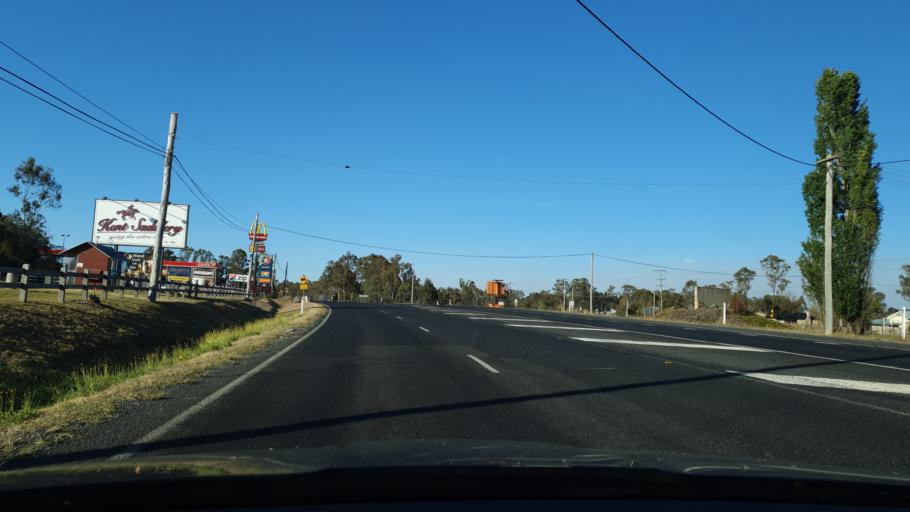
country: AU
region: Queensland
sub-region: Southern Downs
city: Stanthorpe
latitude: -28.6327
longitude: 151.9536
